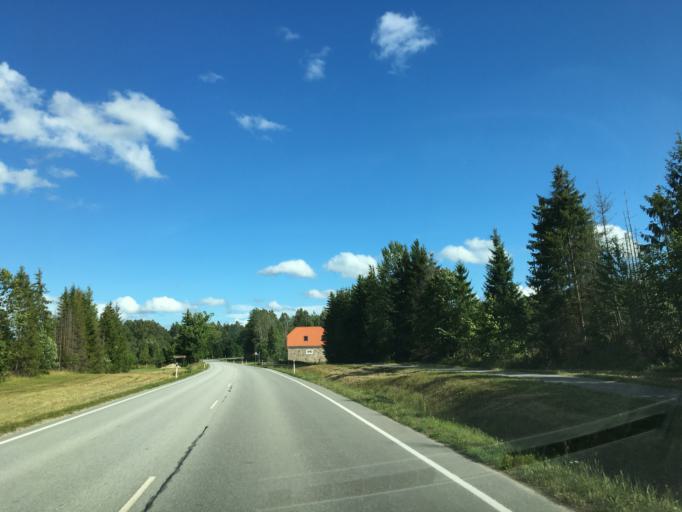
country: EE
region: Paernumaa
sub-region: Vaendra vald (alev)
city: Vandra
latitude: 58.6532
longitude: 25.0592
